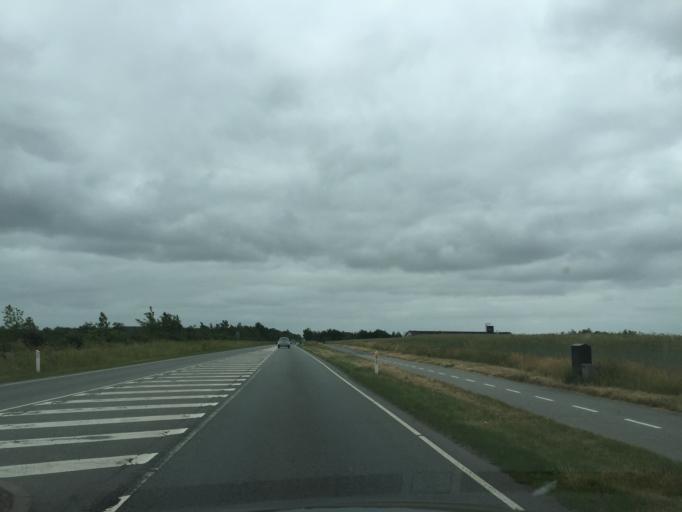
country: DK
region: South Denmark
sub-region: Esbjerg Kommune
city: Ribe
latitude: 55.3139
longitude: 8.7504
